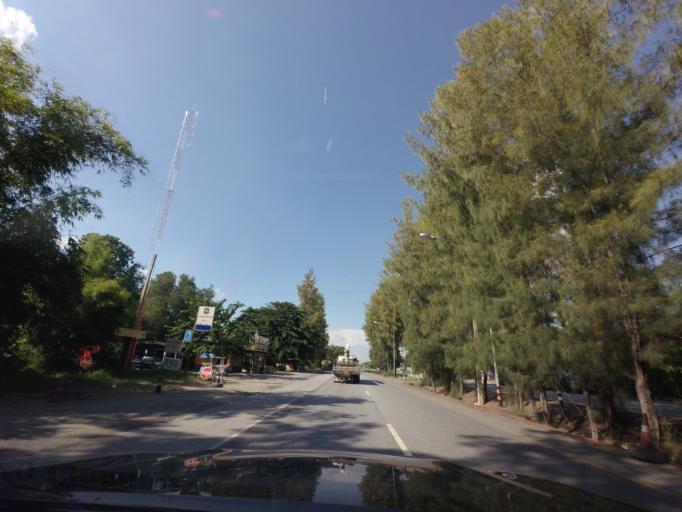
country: TH
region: Nakhon Ratchasima
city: Sida
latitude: 15.5377
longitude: 102.5456
